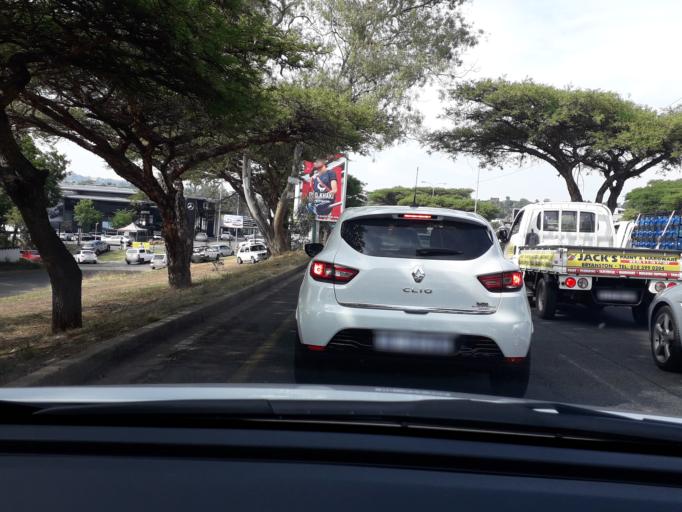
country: ZA
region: Gauteng
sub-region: City of Johannesburg Metropolitan Municipality
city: Johannesburg
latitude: -26.0794
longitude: 28.0256
